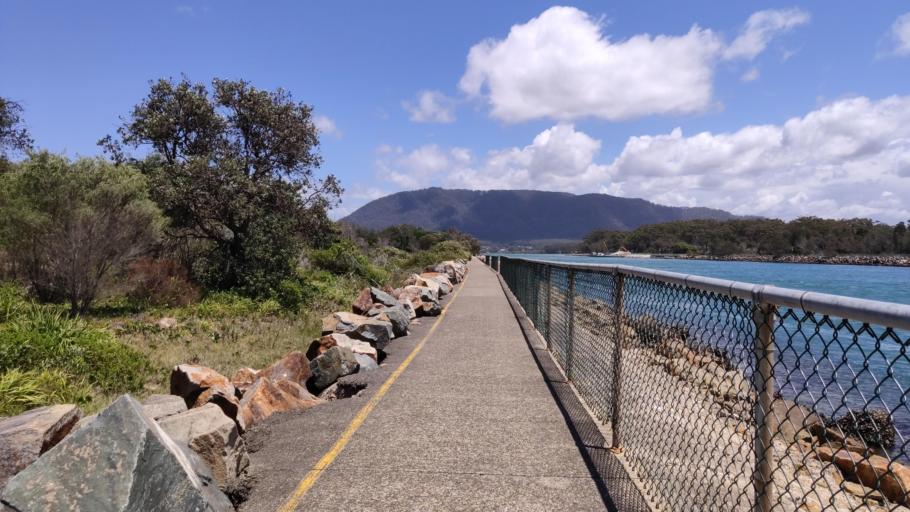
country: AU
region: New South Wales
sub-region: Port Macquarie-Hastings
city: North Haven
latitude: -31.6380
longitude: 152.8320
